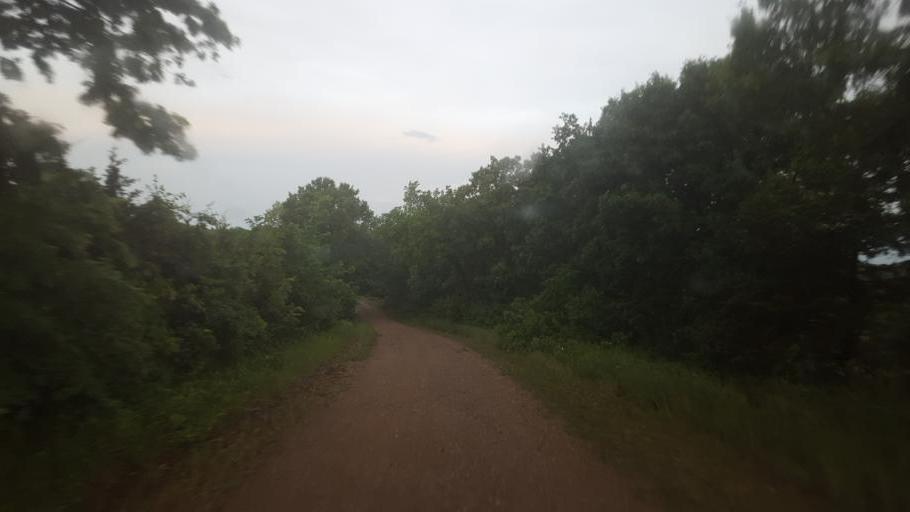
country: US
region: Missouri
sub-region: Moniteau County
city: California
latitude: 38.7249
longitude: -92.6321
